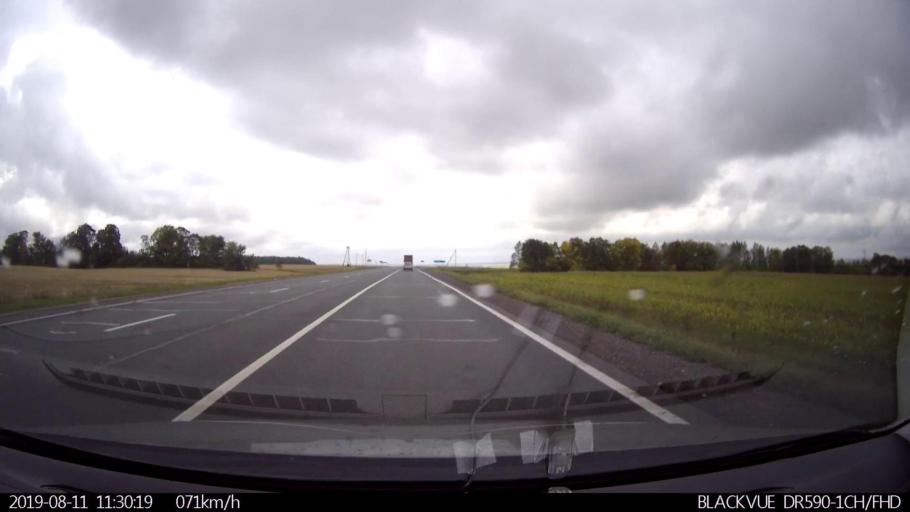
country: RU
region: Ulyanovsk
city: Krasnyy Gulyay
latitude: 54.0599
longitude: 48.2197
